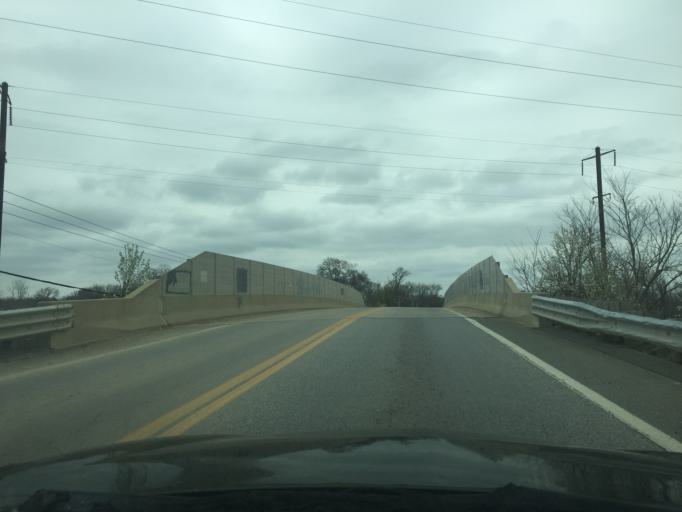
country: US
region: Maryland
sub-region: Baltimore County
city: Bowleys Quarters
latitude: 39.3455
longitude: -76.3942
